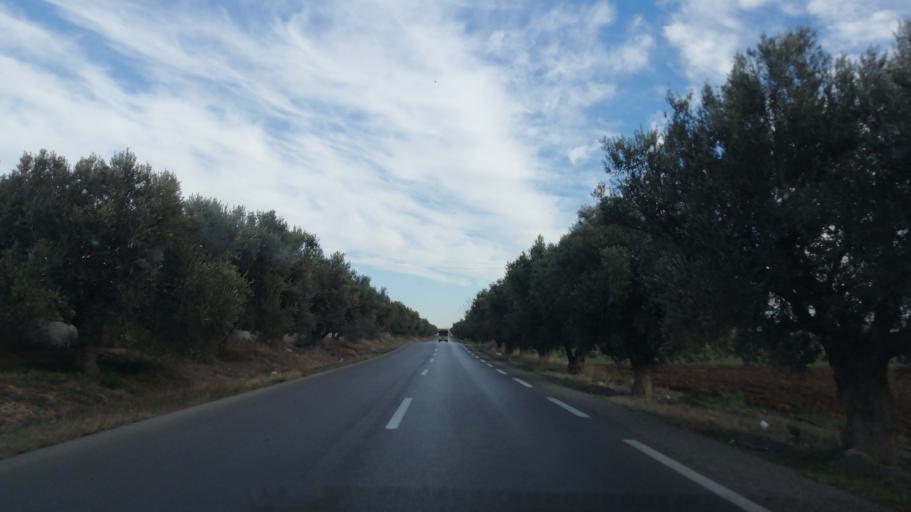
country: DZ
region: Sidi Bel Abbes
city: Sidi Bel Abbes
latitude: 35.1782
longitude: -0.4338
